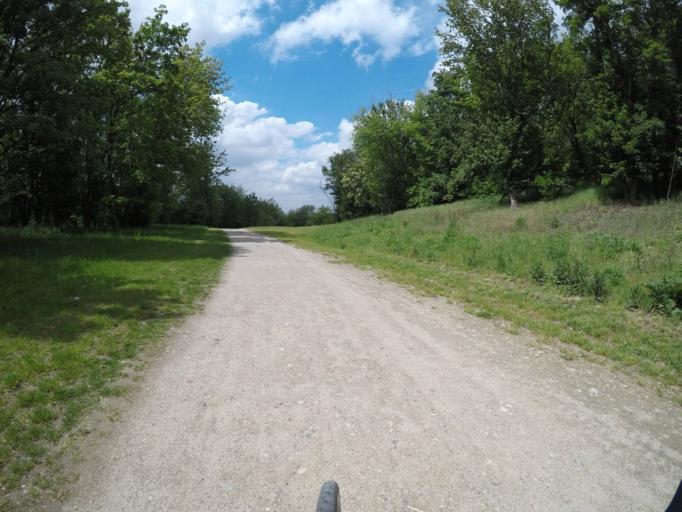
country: DE
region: Berlin
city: Kaulsdorf
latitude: 52.5326
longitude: 13.5813
